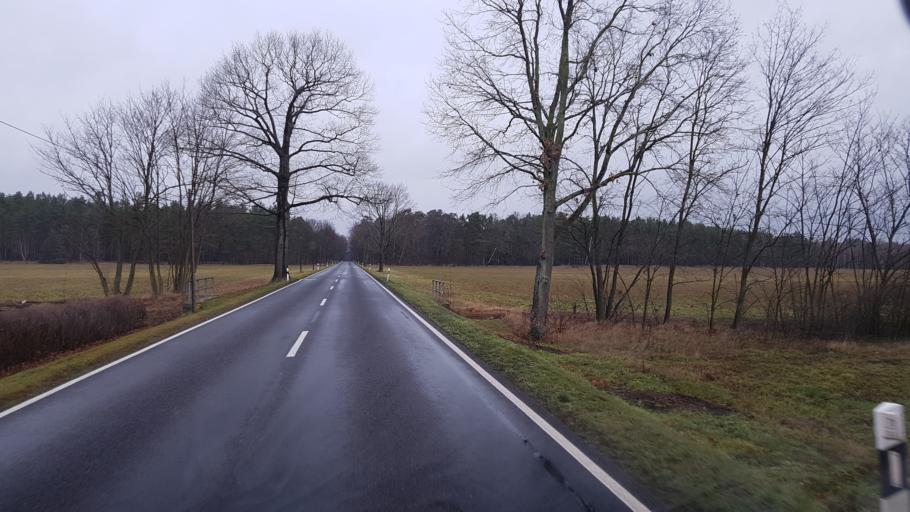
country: DE
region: Brandenburg
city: Altdobern
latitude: 51.6914
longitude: 14.0265
